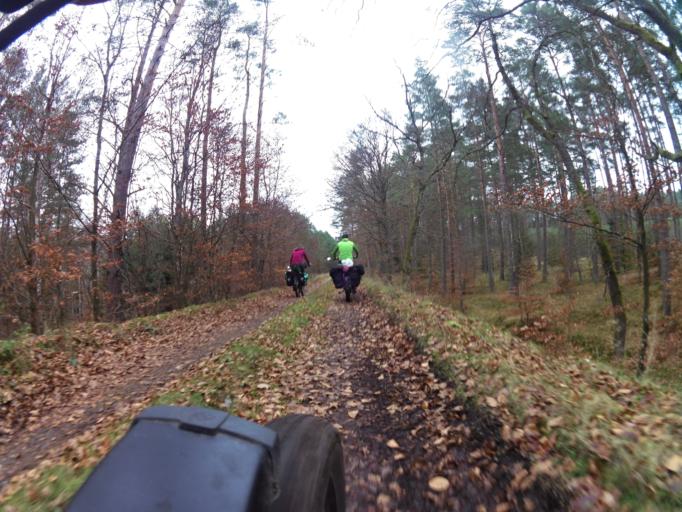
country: PL
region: West Pomeranian Voivodeship
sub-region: Powiat koszalinski
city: Polanow
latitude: 54.0394
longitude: 16.6552
